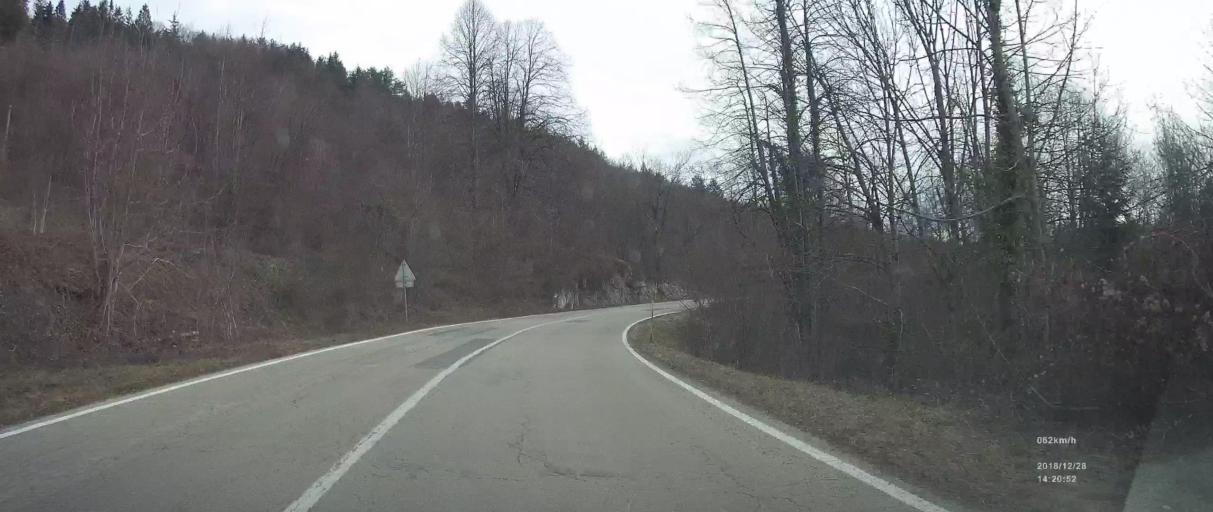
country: HR
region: Primorsko-Goranska
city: Vrbovsko
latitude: 45.3982
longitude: 15.0790
